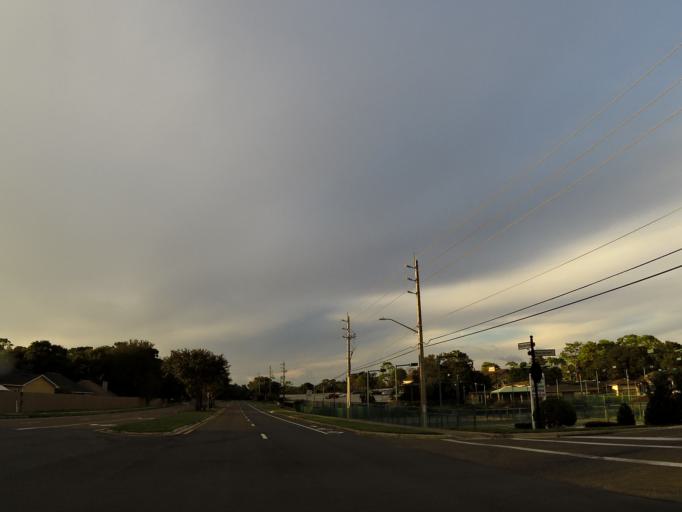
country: US
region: Florida
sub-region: Duval County
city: Atlantic Beach
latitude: 30.3703
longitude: -81.5029
